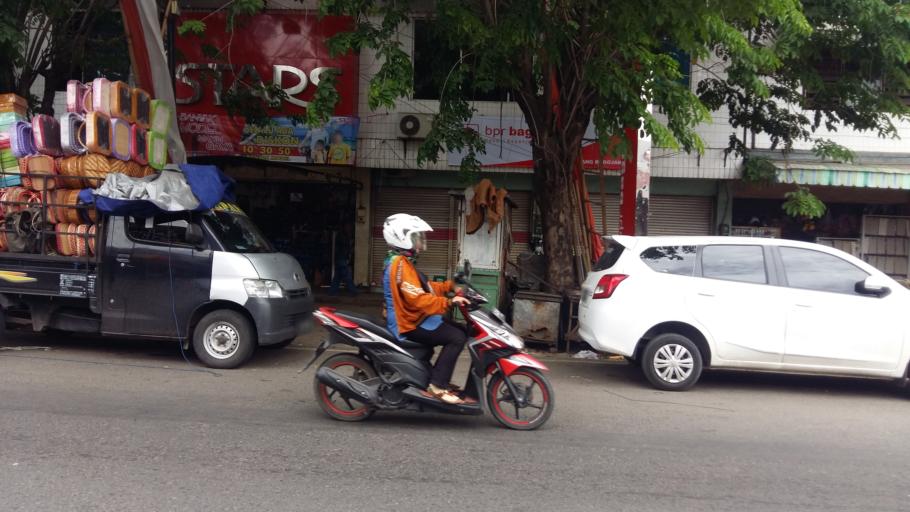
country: ID
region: East Java
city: Krajan
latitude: -8.3076
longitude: 114.2939
